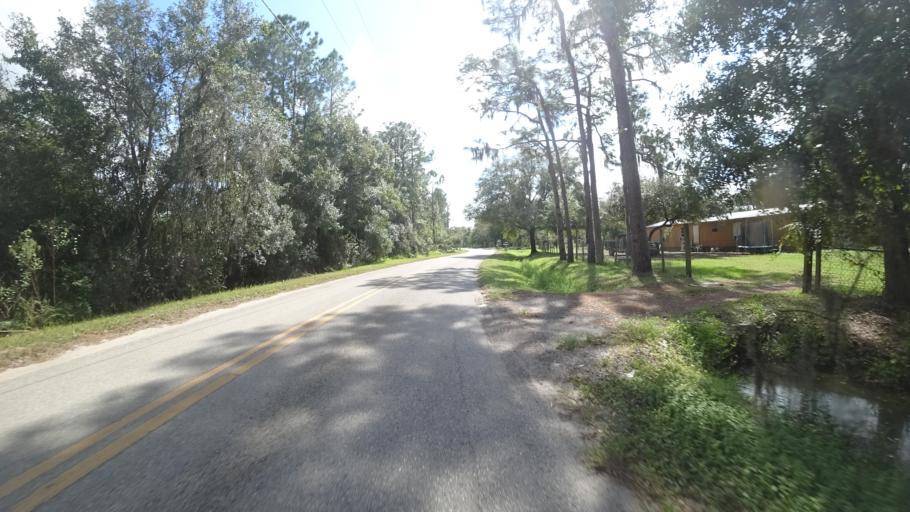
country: US
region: Florida
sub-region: Hillsborough County
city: Sun City Center
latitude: 27.6507
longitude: -82.3608
